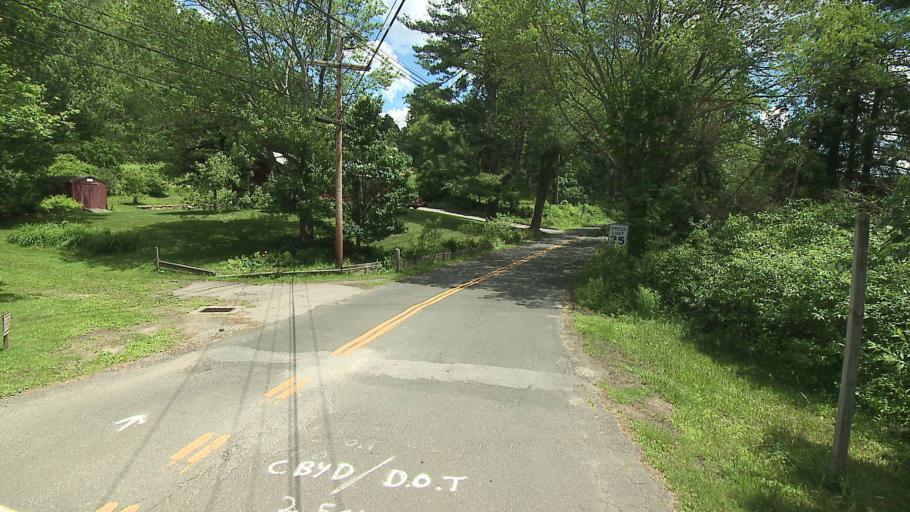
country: US
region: Connecticut
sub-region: Litchfield County
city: New Preston
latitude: 41.7097
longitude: -73.3837
